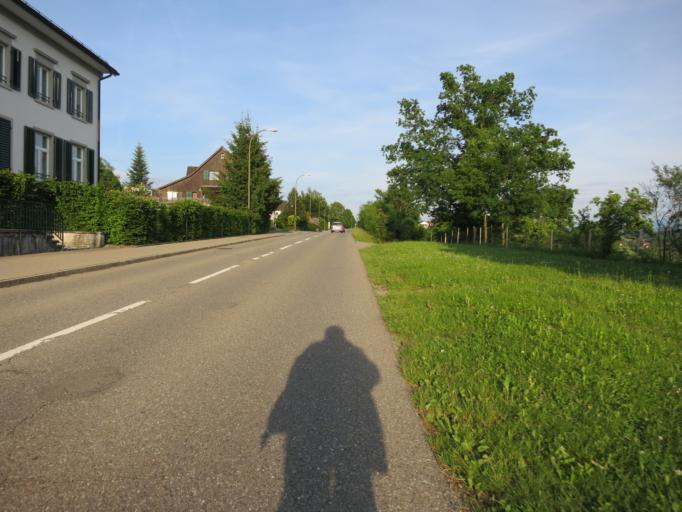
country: CH
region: Zurich
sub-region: Bezirk Hinwil
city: Gossau
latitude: 47.3005
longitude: 8.7643
